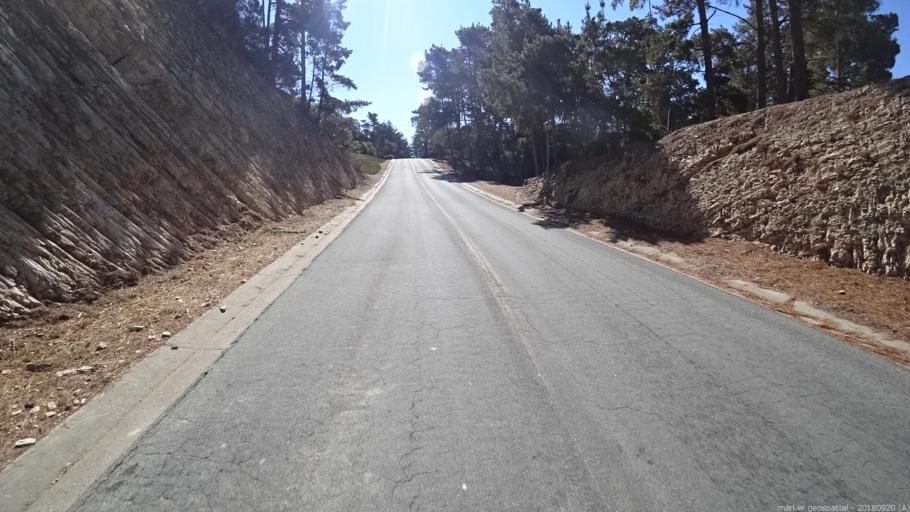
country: US
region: California
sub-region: Monterey County
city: Carmel-by-the-Sea
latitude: 36.5588
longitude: -121.8969
